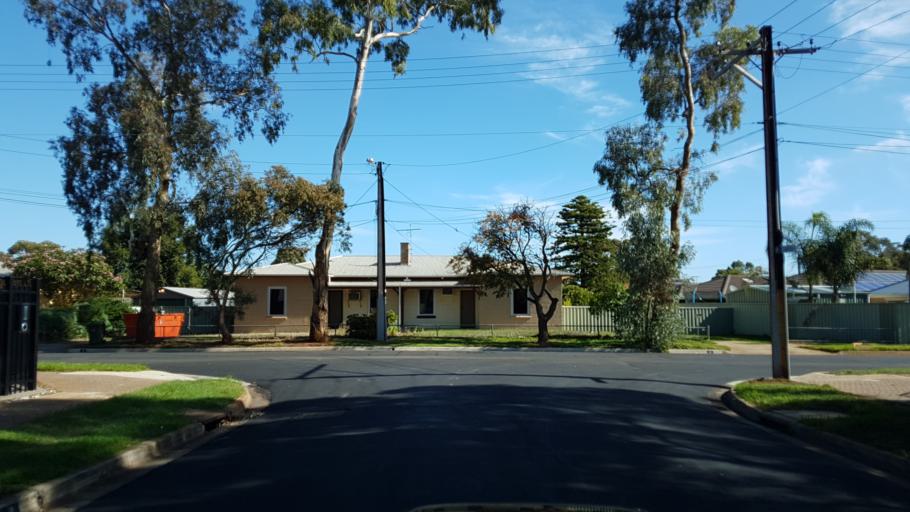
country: AU
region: South Australia
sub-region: Salisbury
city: Salisbury
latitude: -34.7507
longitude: 138.6388
